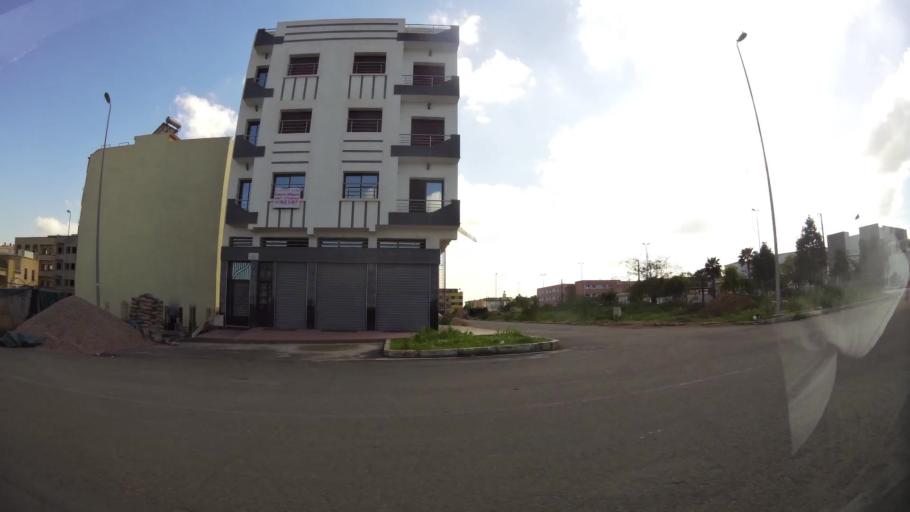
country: MA
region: Grand Casablanca
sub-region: Mediouna
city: Mediouna
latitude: 33.4601
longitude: -7.5159
